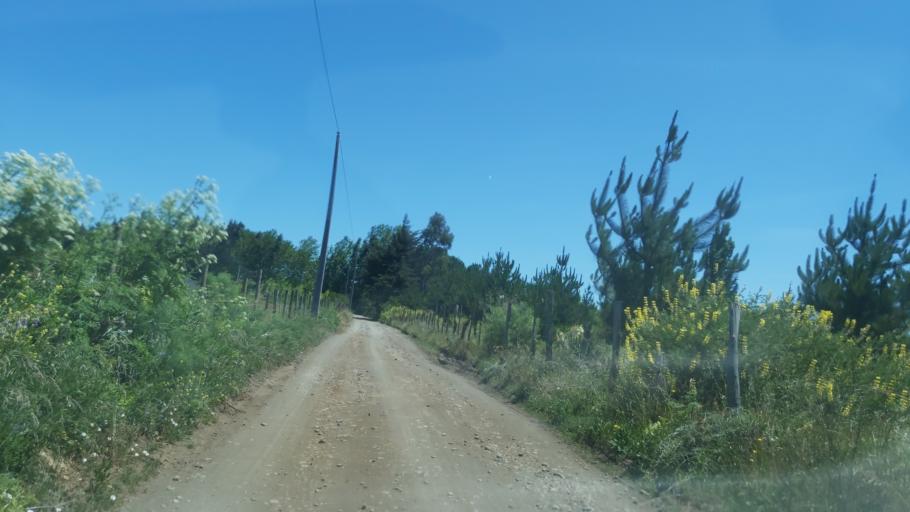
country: CL
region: Maule
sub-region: Provincia de Talca
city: Constitucion
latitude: -35.1631
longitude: -72.2653
